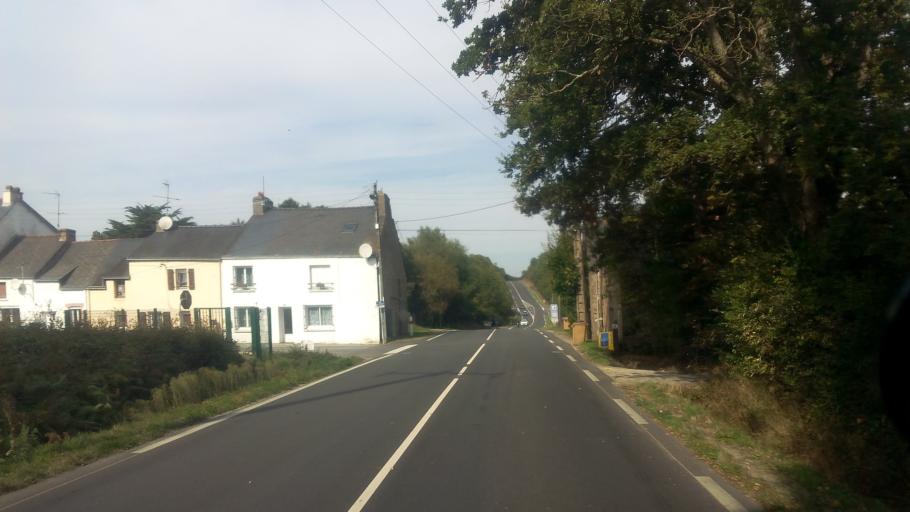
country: FR
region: Brittany
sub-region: Departement d'Ille-et-Vilaine
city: Redon
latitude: 47.6762
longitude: -2.0823
